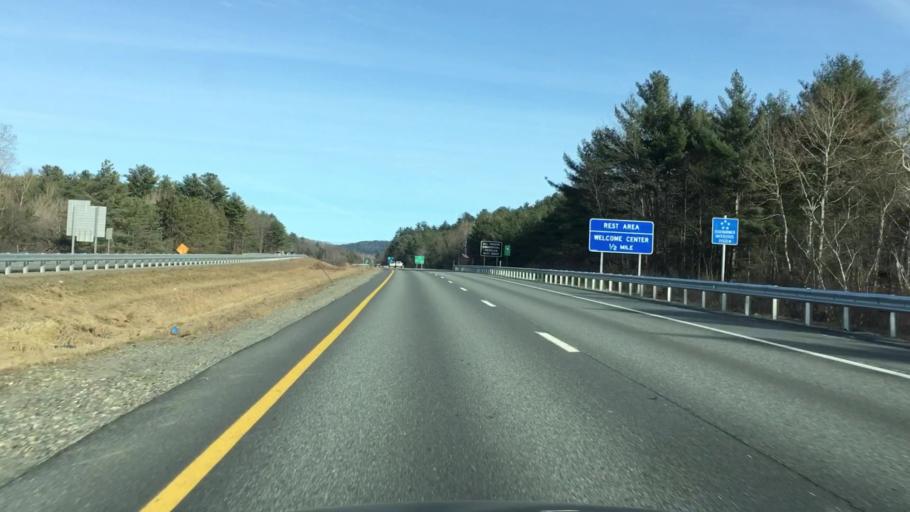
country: US
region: New Hampshire
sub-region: Grafton County
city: Lebanon
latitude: 43.6432
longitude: -72.2714
